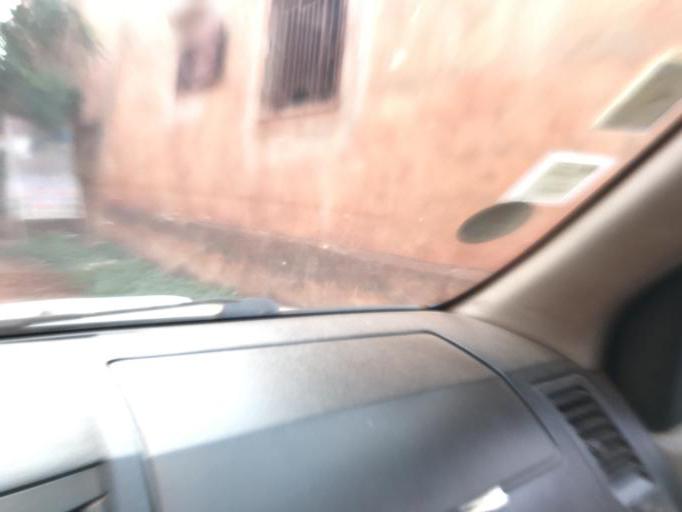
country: ML
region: Bamako
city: Bamako
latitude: 12.5813
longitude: -8.0040
